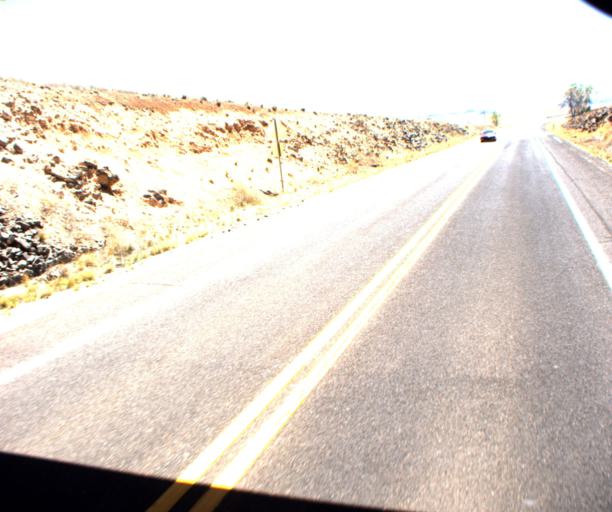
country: US
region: Arizona
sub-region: Yavapai County
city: Paulden
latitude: 35.3196
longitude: -112.8496
